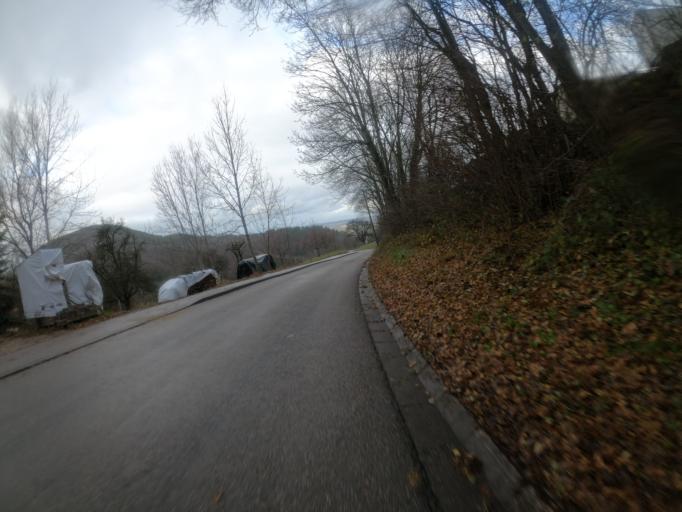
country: DE
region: Baden-Wuerttemberg
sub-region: Regierungsbezirk Stuttgart
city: Waldstetten
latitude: 48.7359
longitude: 9.8405
